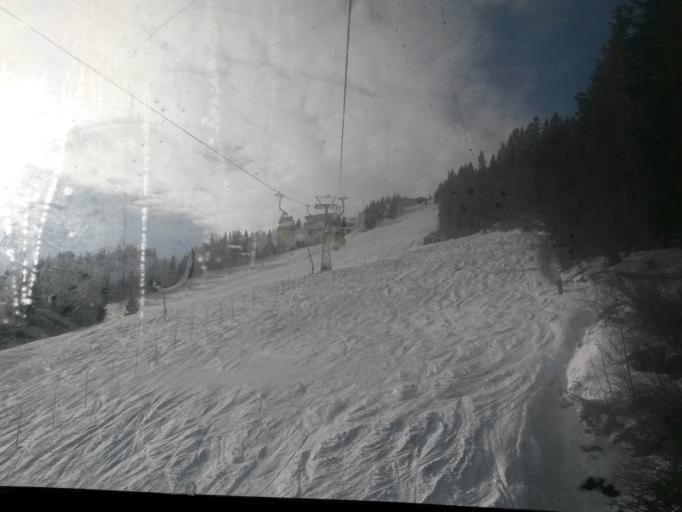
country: AT
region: Salzburg
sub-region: Politischer Bezirk Sankt Johann im Pongau
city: Dorfgastein
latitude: 47.2358
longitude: 13.1776
